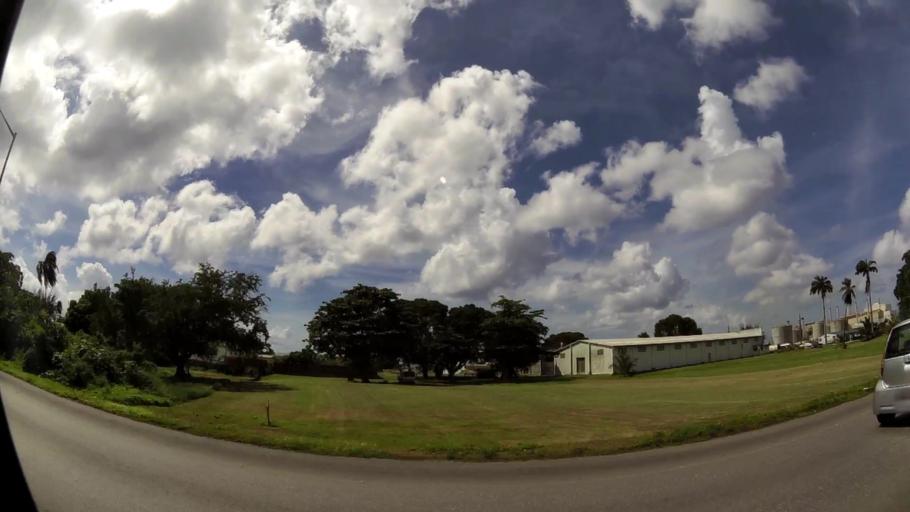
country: BB
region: Saint Michael
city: Bridgetown
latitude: 13.1230
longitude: -59.6284
